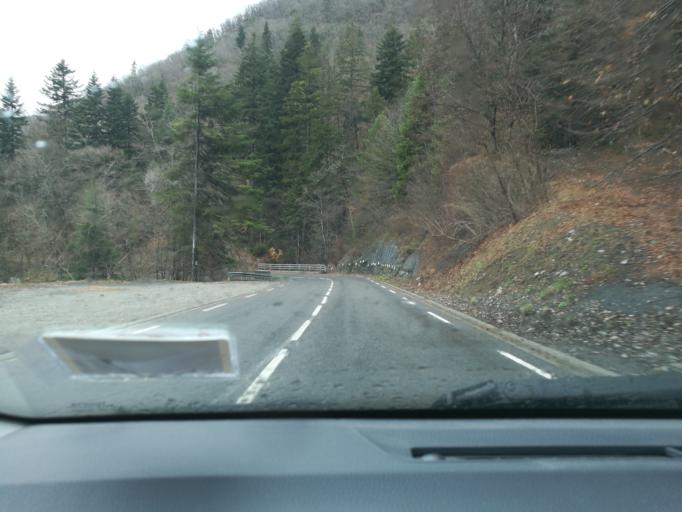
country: FR
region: Rhone-Alpes
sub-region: Departement de la Haute-Savoie
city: Araches-la-Frasse
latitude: 46.0446
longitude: 6.6117
